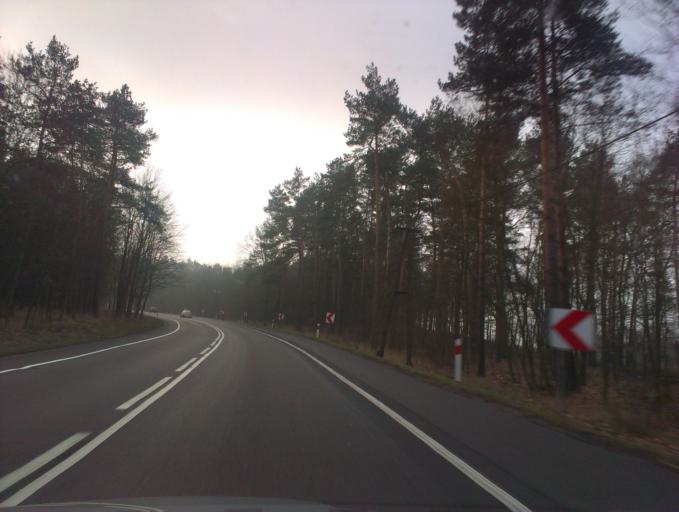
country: PL
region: Greater Poland Voivodeship
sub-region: Powiat chodzieski
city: Budzyn
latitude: 52.8467
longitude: 16.9698
